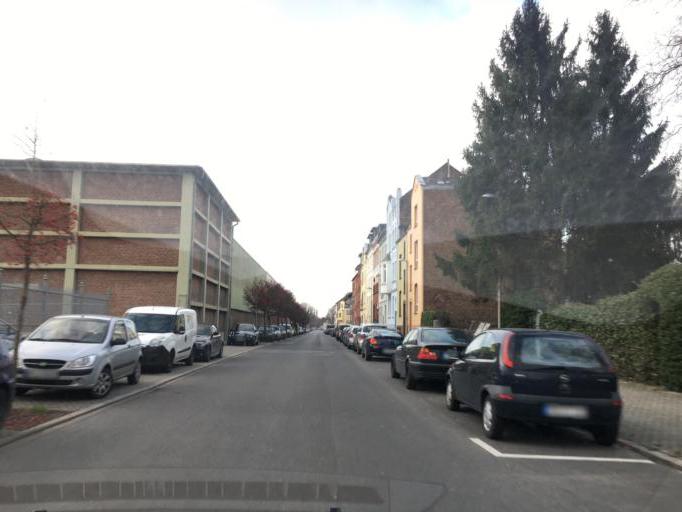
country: DE
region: North Rhine-Westphalia
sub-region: Regierungsbezirk Koln
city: Dueren
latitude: 50.8043
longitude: 6.4749
